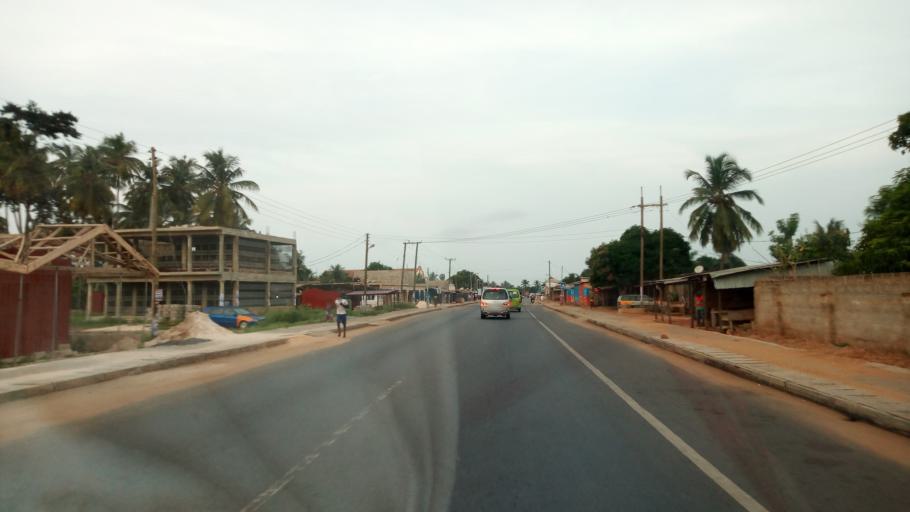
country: TG
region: Maritime
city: Lome
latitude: 6.1112
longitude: 1.1604
